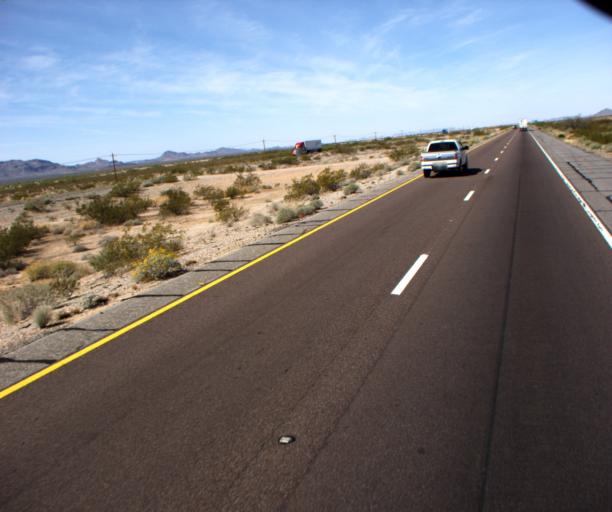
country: US
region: Arizona
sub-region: La Paz County
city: Salome
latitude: 33.5647
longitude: -113.3226
